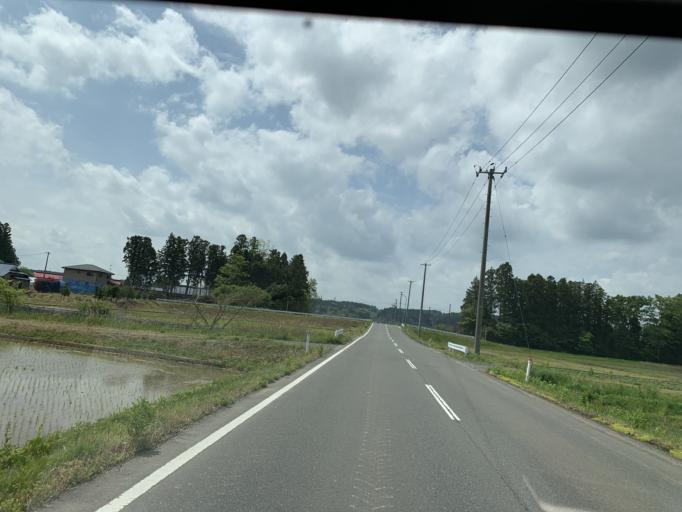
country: JP
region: Miyagi
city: Furukawa
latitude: 38.7506
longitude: 140.9358
